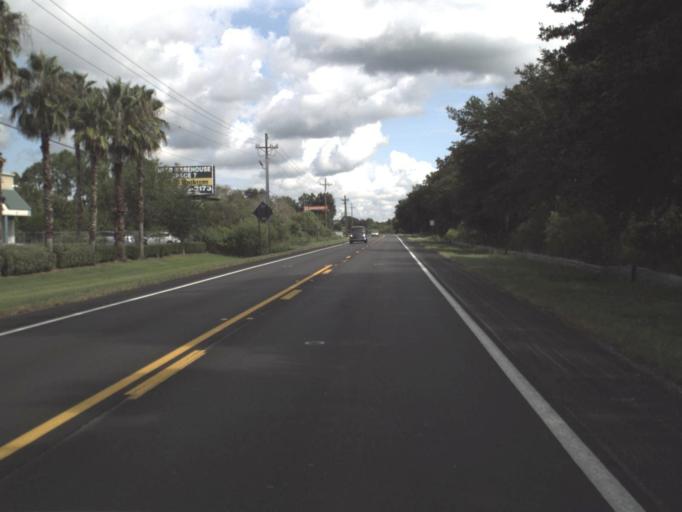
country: US
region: Florida
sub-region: Polk County
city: Combee Settlement
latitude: 28.1040
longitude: -81.9056
